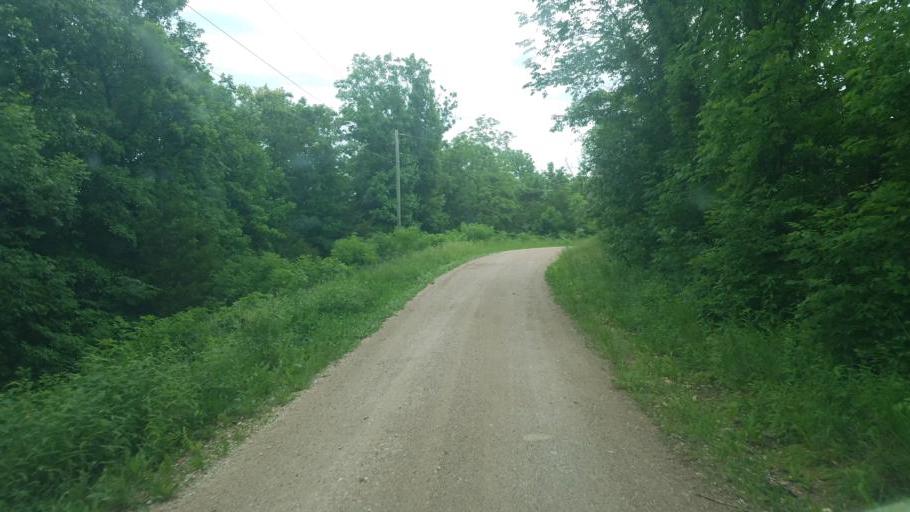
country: US
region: Missouri
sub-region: Moniteau County
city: California
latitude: 38.6110
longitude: -92.6469
